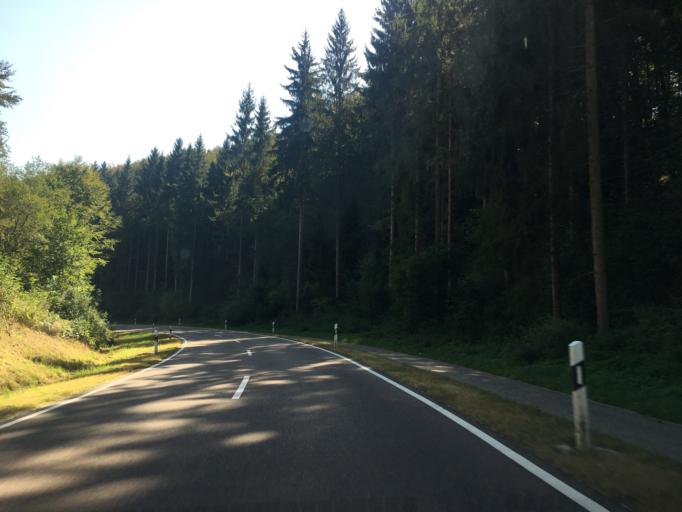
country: DE
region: Baden-Wuerttemberg
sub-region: Tuebingen Region
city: Munsingen
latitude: 48.3764
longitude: 9.4822
